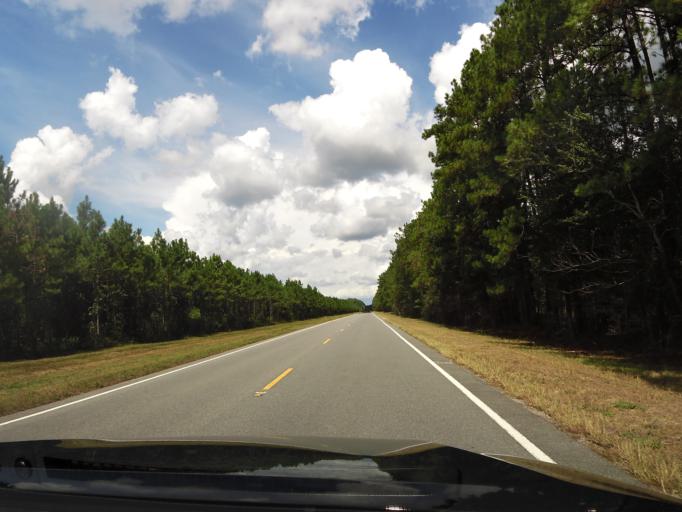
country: US
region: Georgia
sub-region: Charlton County
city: Folkston
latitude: 30.9908
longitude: -82.0261
